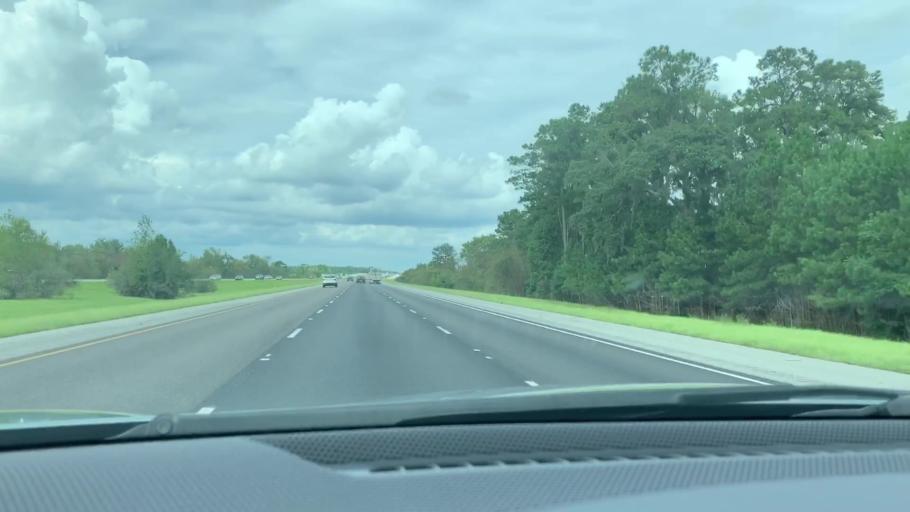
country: US
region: Georgia
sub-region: Liberty County
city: Midway
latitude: 31.7269
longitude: -81.3883
